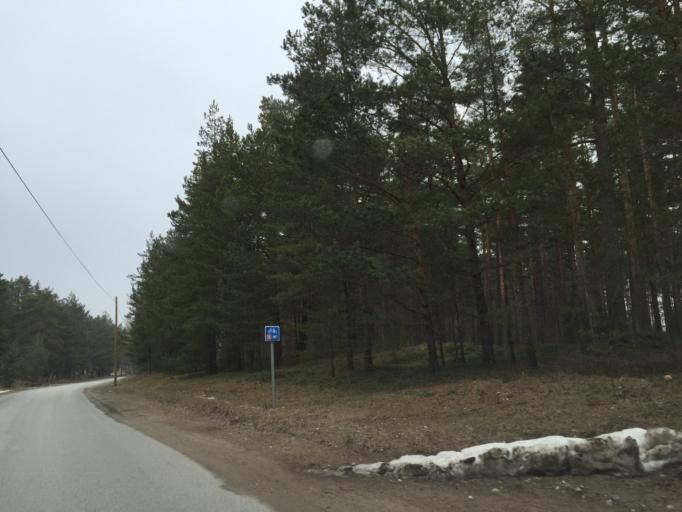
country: LV
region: Salacgrivas
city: Ainazi
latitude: 58.0215
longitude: 24.4544
